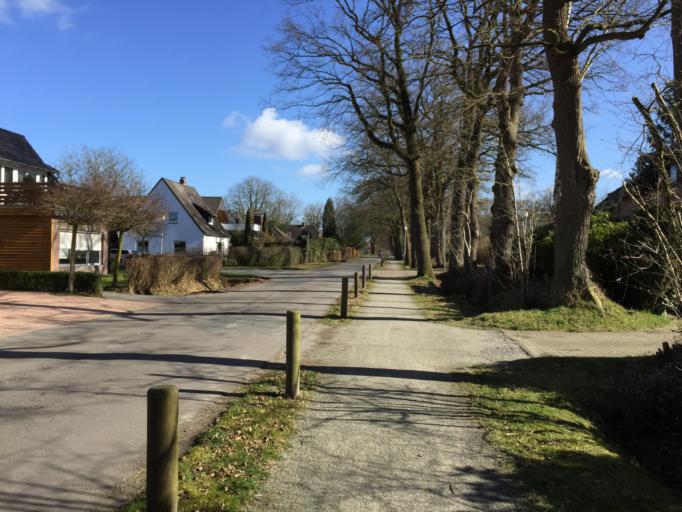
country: DE
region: Lower Saxony
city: Oldenburg
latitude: 53.1747
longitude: 8.2322
